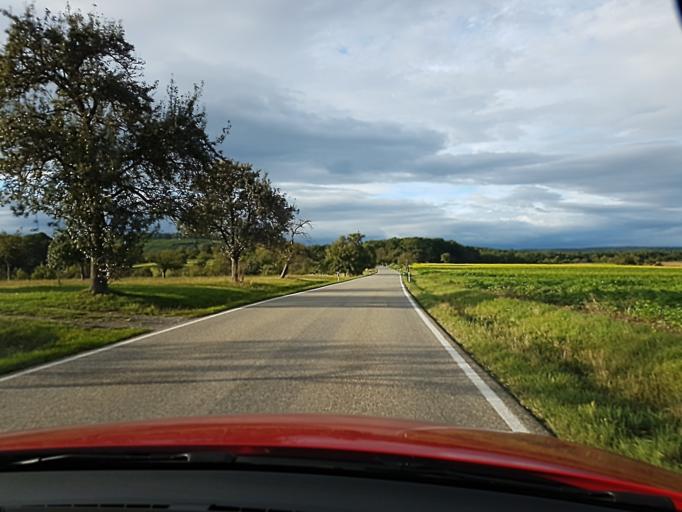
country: DE
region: Baden-Wuerttemberg
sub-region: Karlsruhe Region
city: Muhlacker
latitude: 48.9847
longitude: 8.8635
